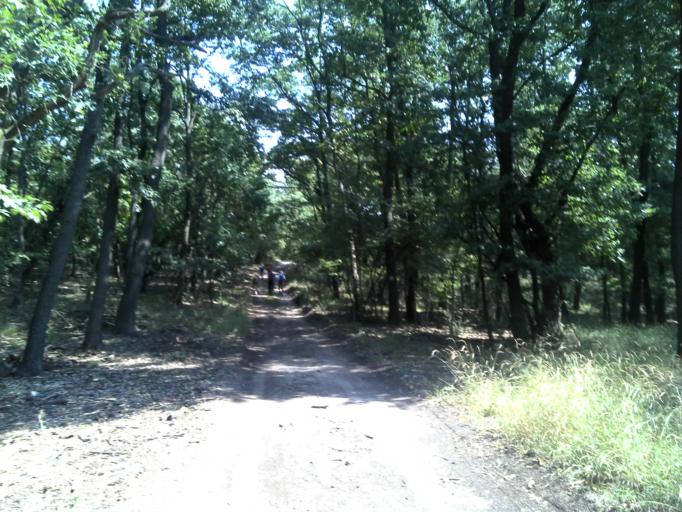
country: HU
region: Komarom-Esztergom
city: Oroszlany
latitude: 47.4400
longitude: 18.3831
